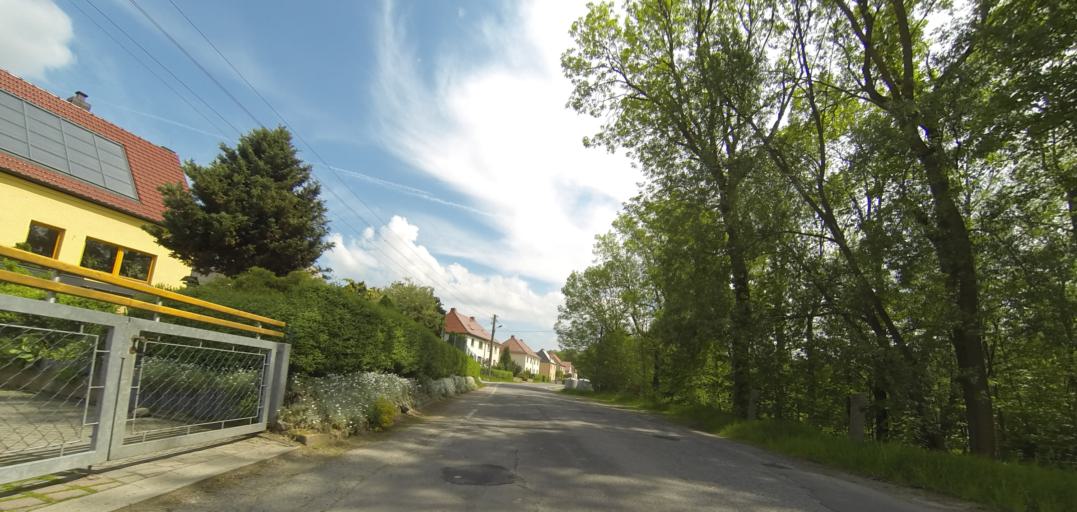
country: DE
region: Saxony
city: Grossharthau
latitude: 51.0978
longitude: 14.0486
